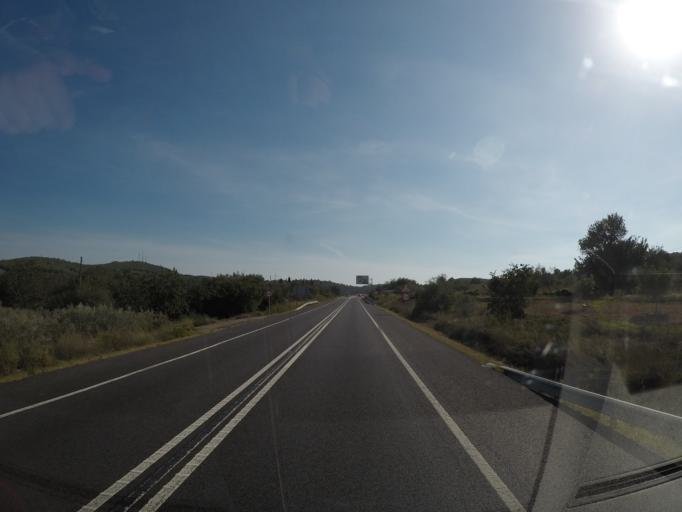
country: ES
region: Catalonia
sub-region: Provincia de Tarragona
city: El Perello
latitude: 40.8849
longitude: 0.7188
